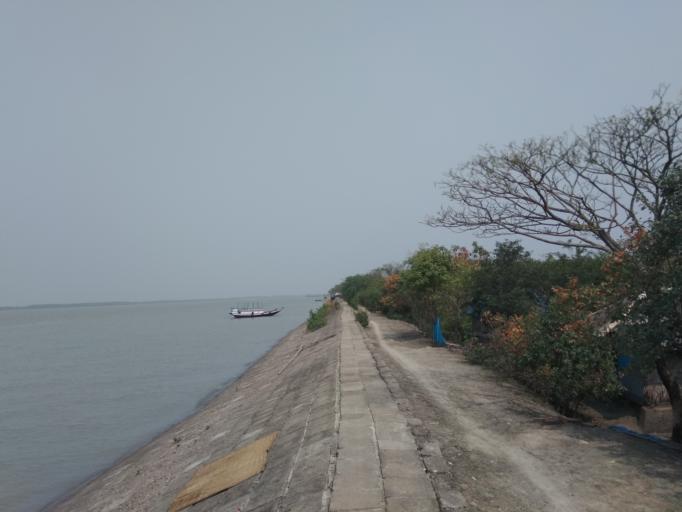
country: IN
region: West Bengal
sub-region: North 24 Parganas
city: Gosaba
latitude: 22.2520
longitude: 89.2503
